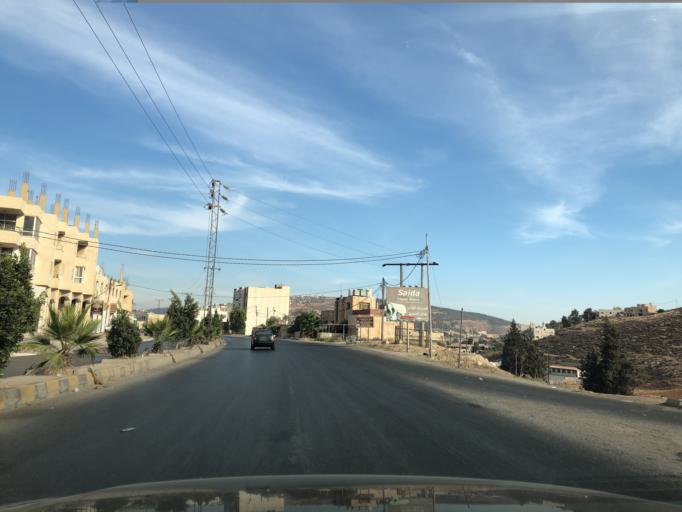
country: JO
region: Jerash
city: Jarash
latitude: 32.2705
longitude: 35.8825
